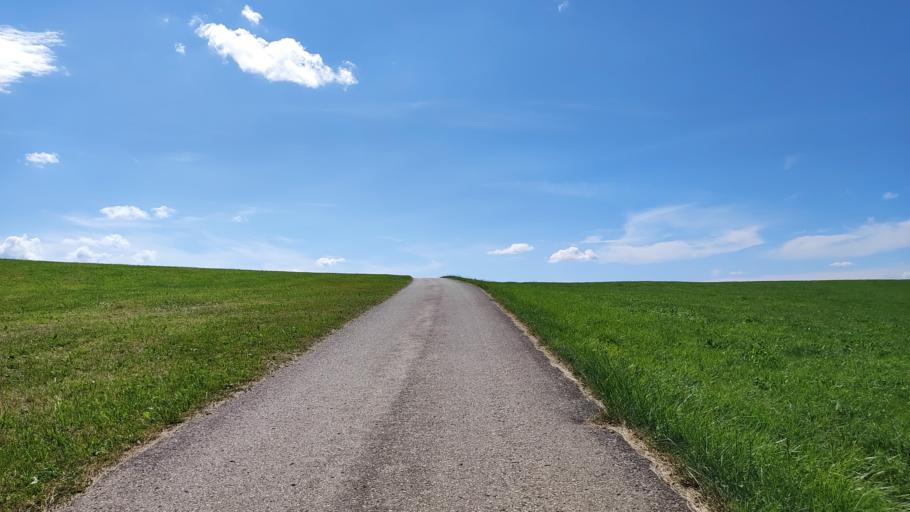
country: DE
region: Bavaria
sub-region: Swabia
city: Obergunzburg
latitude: 47.8400
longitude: 10.4329
